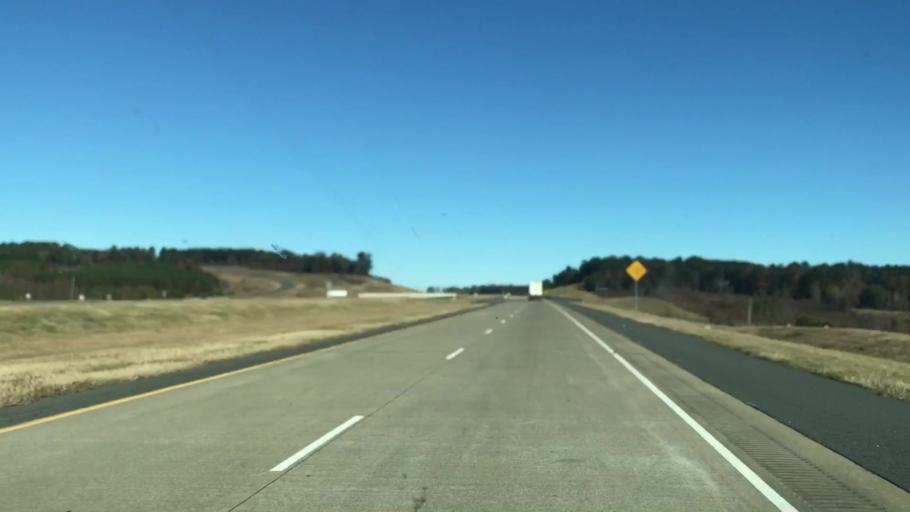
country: US
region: Louisiana
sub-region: Caddo Parish
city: Vivian
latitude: 32.9406
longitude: -93.8972
